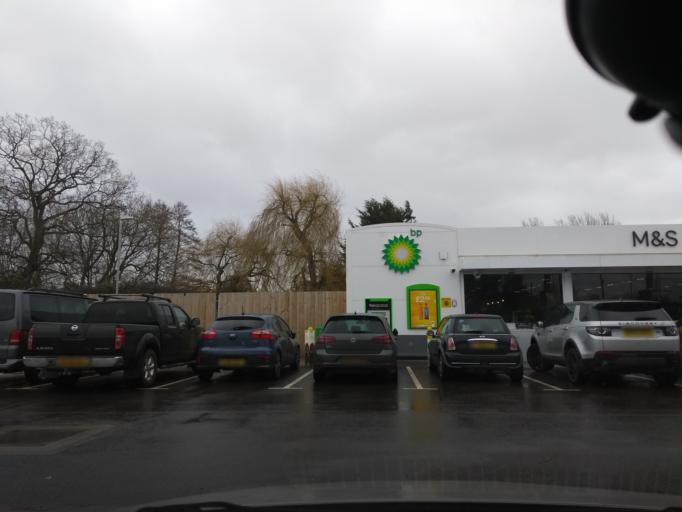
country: GB
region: England
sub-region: Somerset
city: Taunton
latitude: 51.0318
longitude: -3.1363
